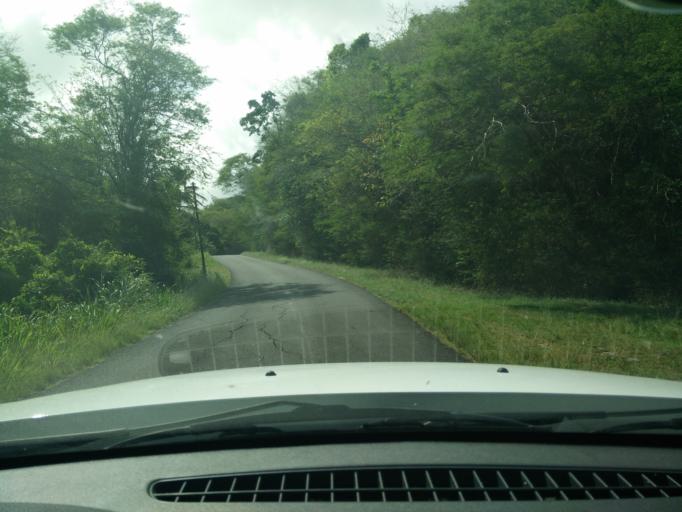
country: GP
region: Guadeloupe
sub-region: Guadeloupe
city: Le Gosier
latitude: 16.2249
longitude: -61.4558
